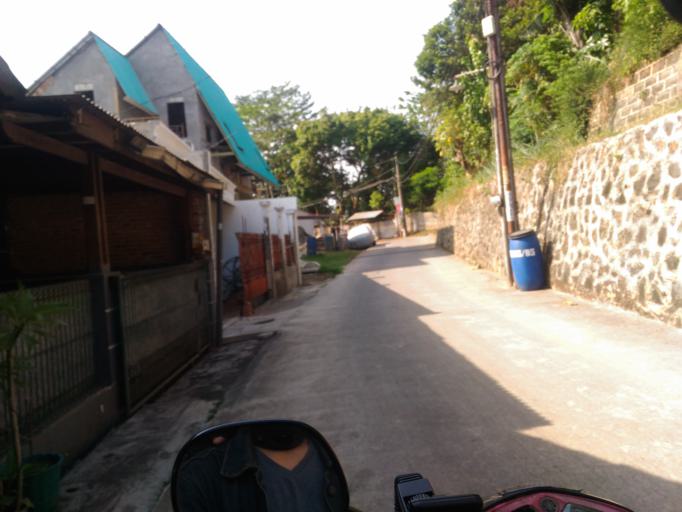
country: ID
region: West Java
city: Depok
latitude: -6.3438
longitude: 106.8403
